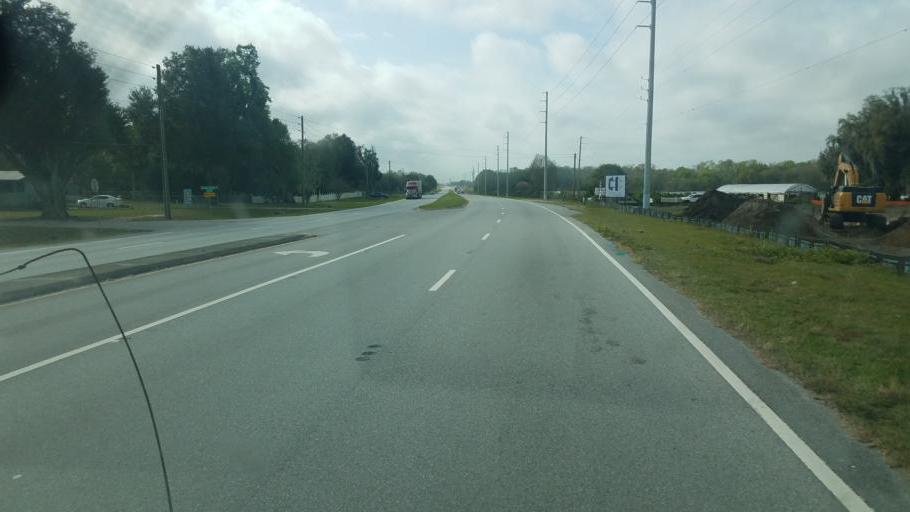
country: US
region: Florida
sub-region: Polk County
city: Winston
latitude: 27.9902
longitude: -82.0559
